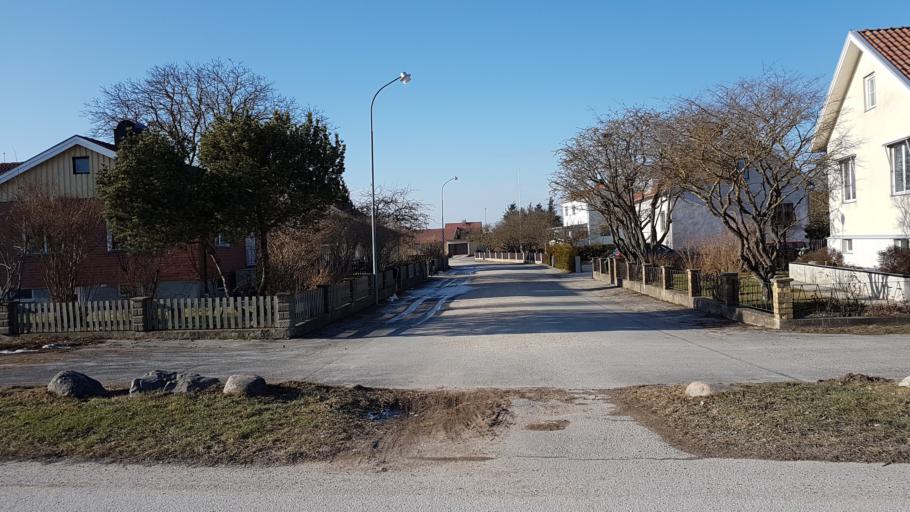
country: SE
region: Gotland
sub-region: Gotland
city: Visby
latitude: 57.6331
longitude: 18.3196
